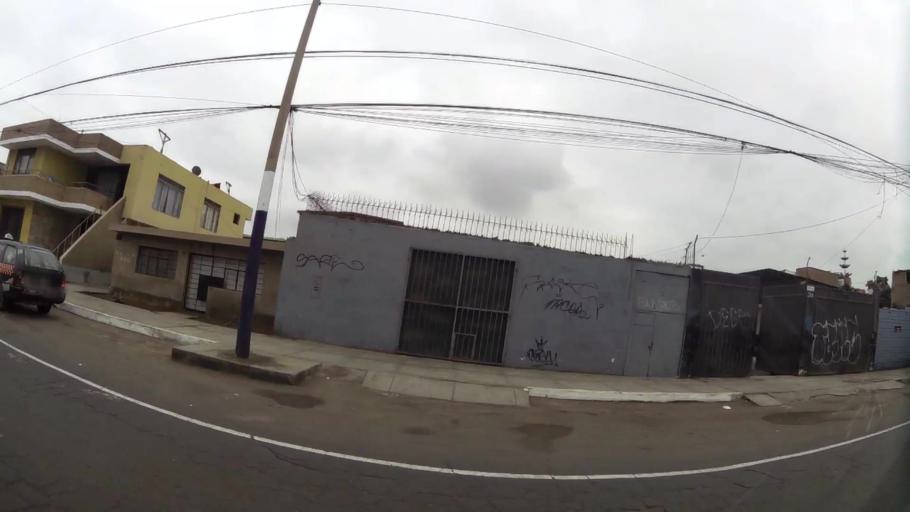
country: PE
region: Lima
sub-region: Lima
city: Surco
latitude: -12.1983
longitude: -77.0005
